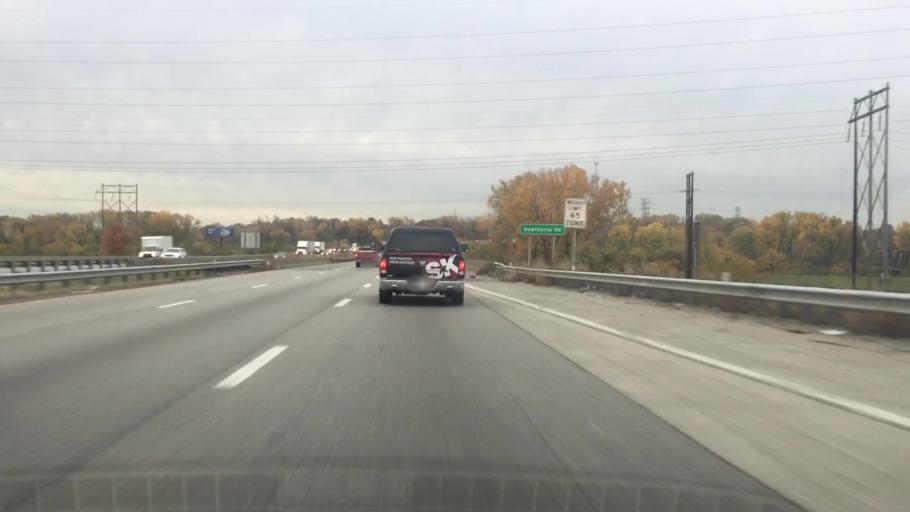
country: US
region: Missouri
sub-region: Jackson County
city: Sugar Creek
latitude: 39.1215
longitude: -94.4927
